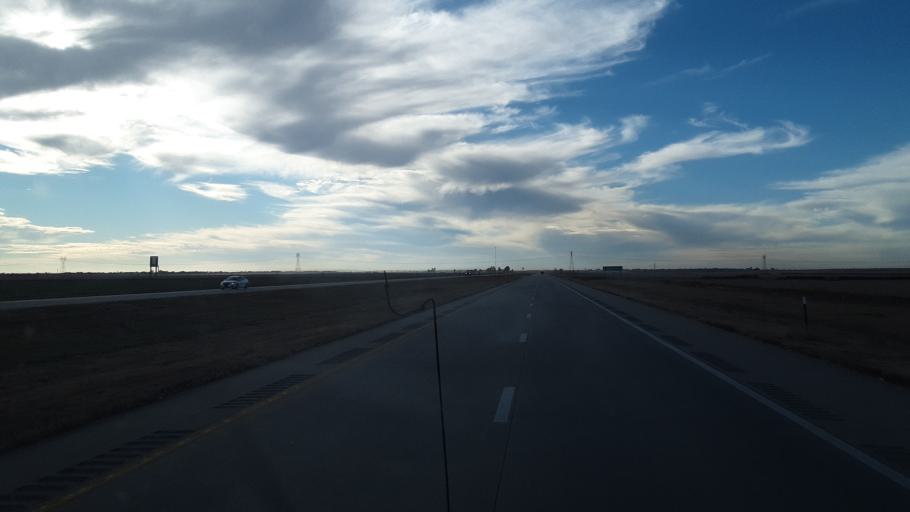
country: US
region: Kansas
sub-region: Finney County
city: Holcomb
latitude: 38.0034
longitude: -100.9532
